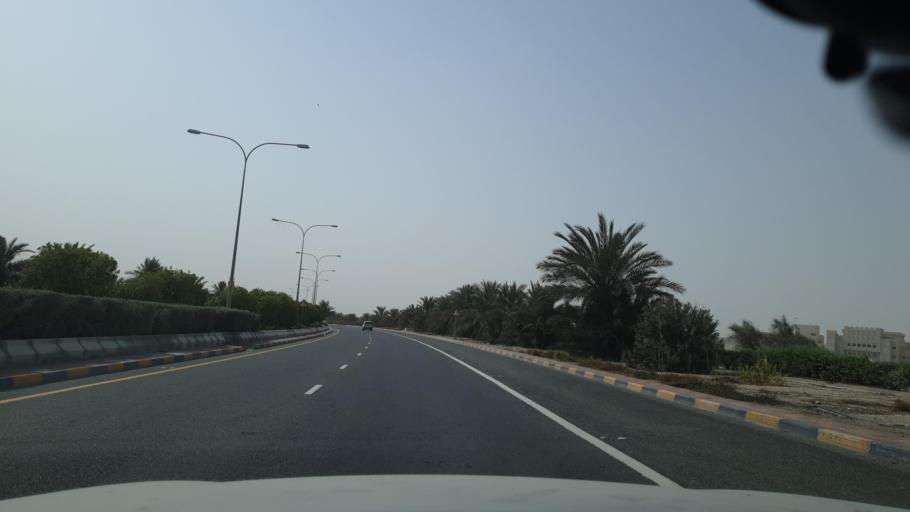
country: QA
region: Al Wakrah
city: Umm Sa'id
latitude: 25.0082
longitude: 51.5588
